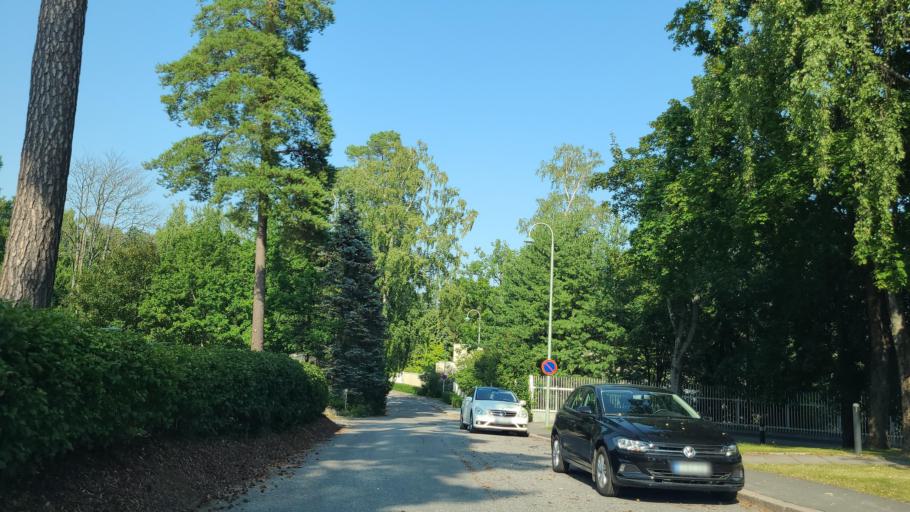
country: FI
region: Uusimaa
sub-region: Helsinki
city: Teekkarikylae
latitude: 60.1857
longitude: 24.8654
